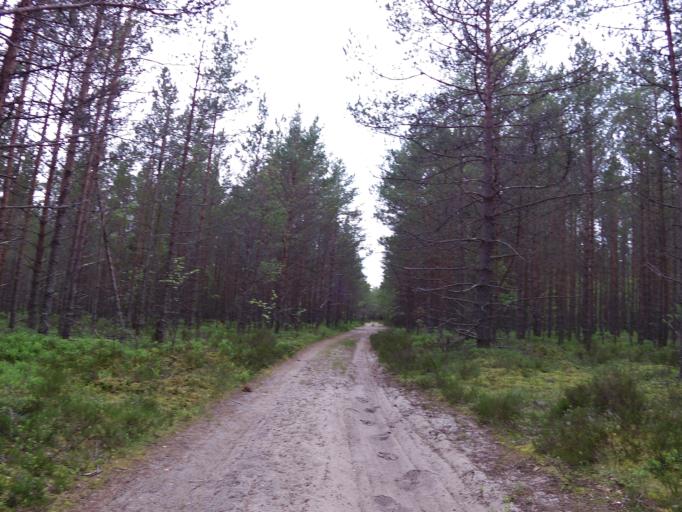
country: EE
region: Harju
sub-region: Paldiski linn
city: Paldiski
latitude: 59.2432
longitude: 23.7467
